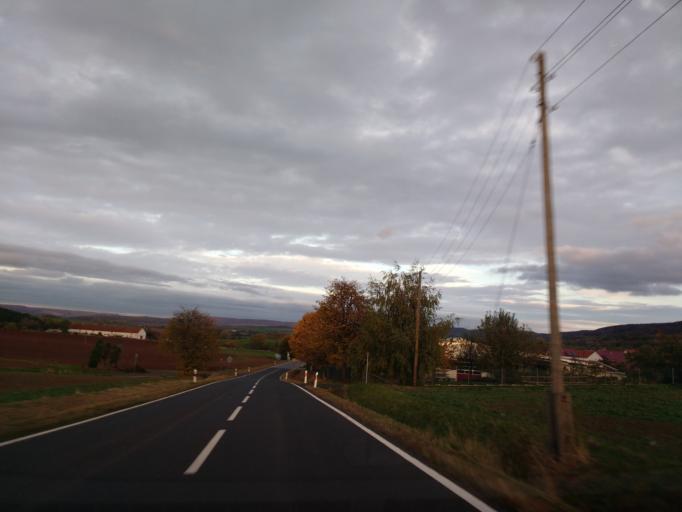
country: DE
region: Thuringia
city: Kleinbartloff
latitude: 51.3530
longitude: 10.3792
